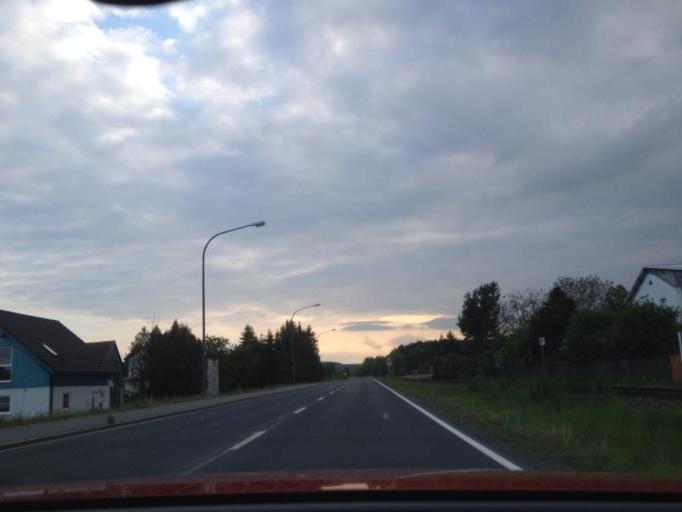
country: DE
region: Bavaria
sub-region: Upper Palatinate
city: Hirschau
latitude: 49.5394
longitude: 11.9289
